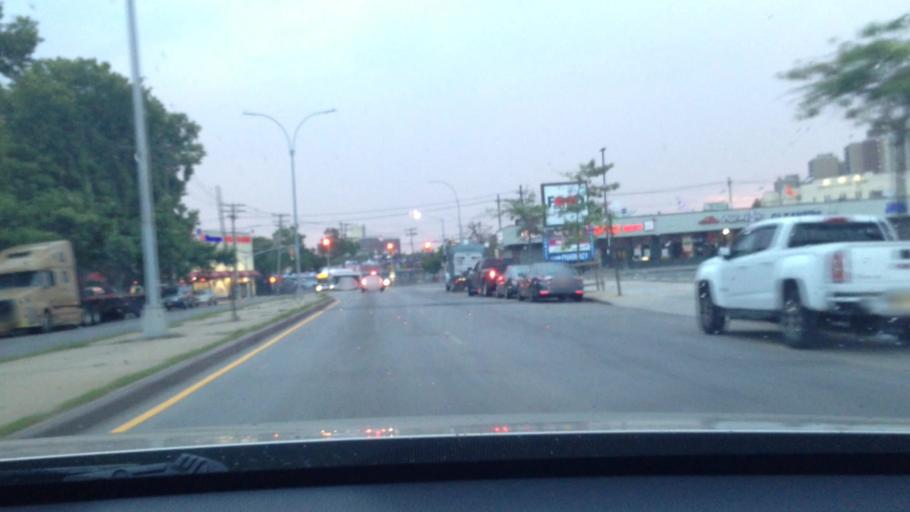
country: US
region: New York
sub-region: Kings County
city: East New York
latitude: 40.6502
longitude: -73.8910
